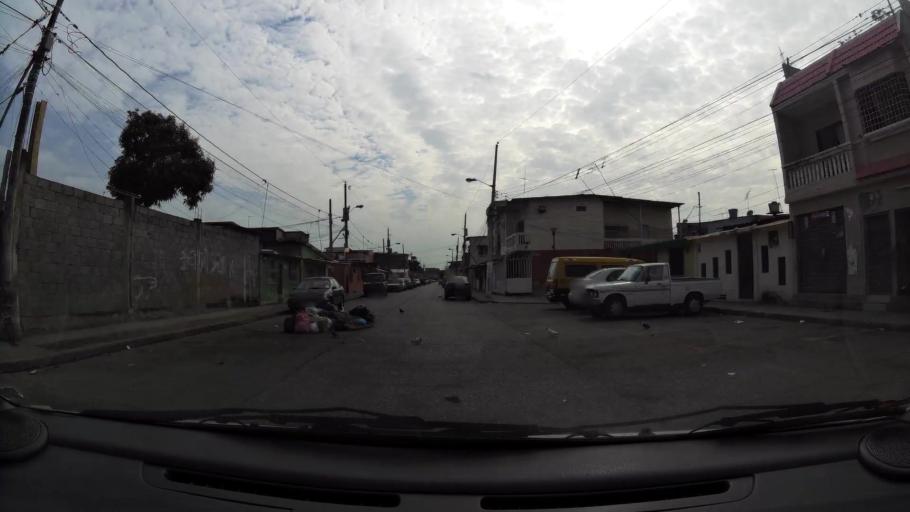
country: EC
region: Guayas
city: Guayaquil
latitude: -2.2554
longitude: -79.8861
